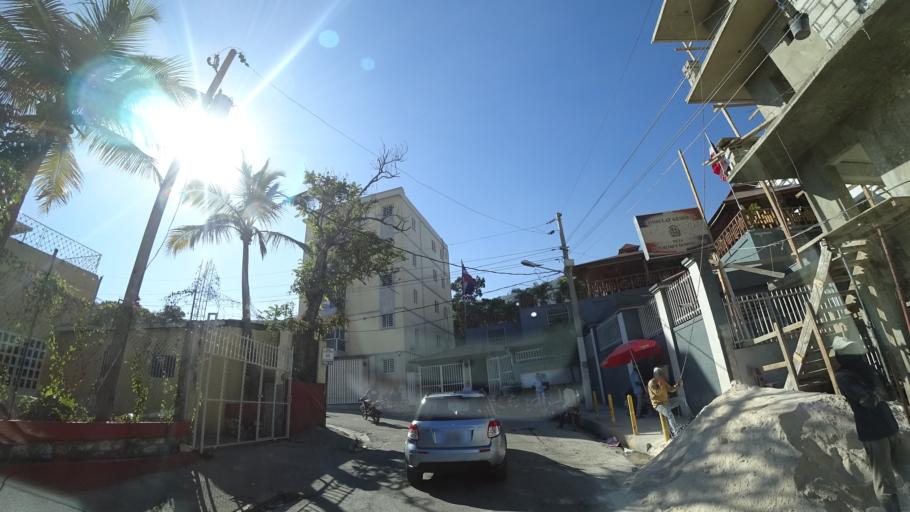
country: HT
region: Ouest
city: Petionville
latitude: 18.5156
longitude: -72.2935
